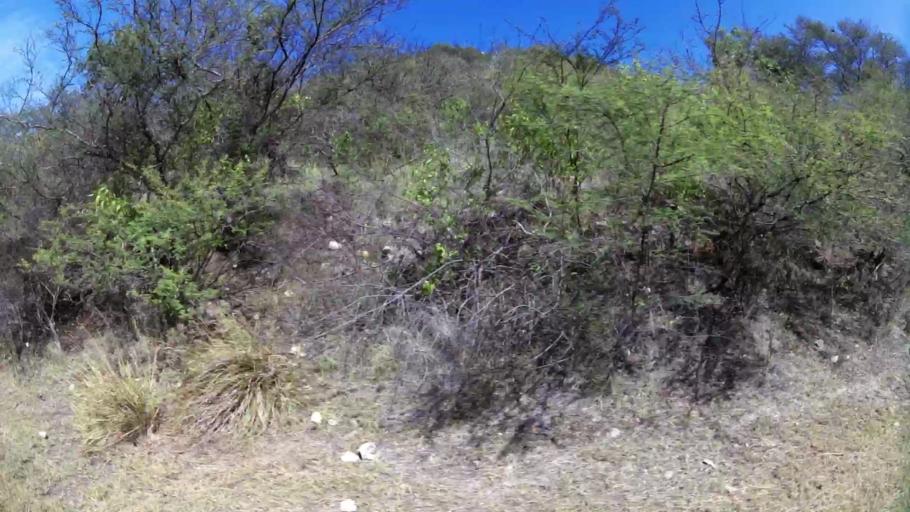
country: AG
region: Saint Paul
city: Falmouth
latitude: 17.0195
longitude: -61.7401
